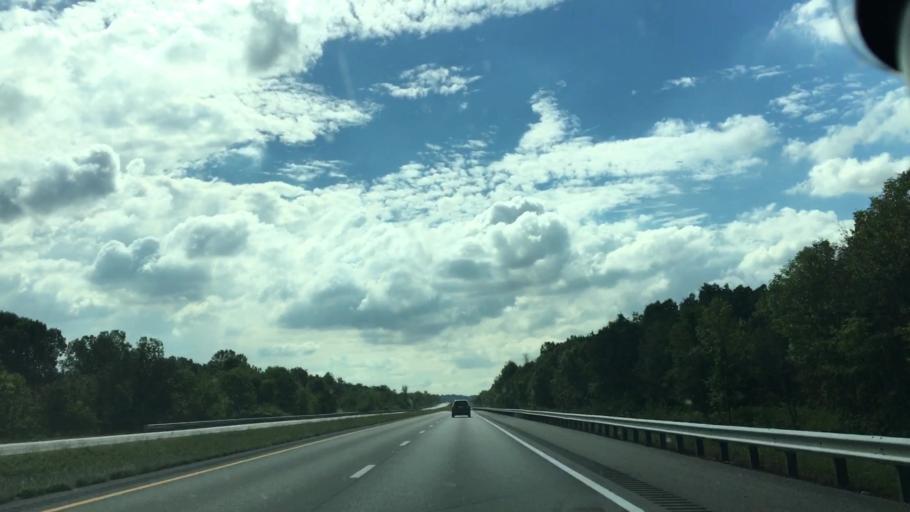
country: US
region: Kentucky
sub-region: Webster County
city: Sebree
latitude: 37.5902
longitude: -87.4917
